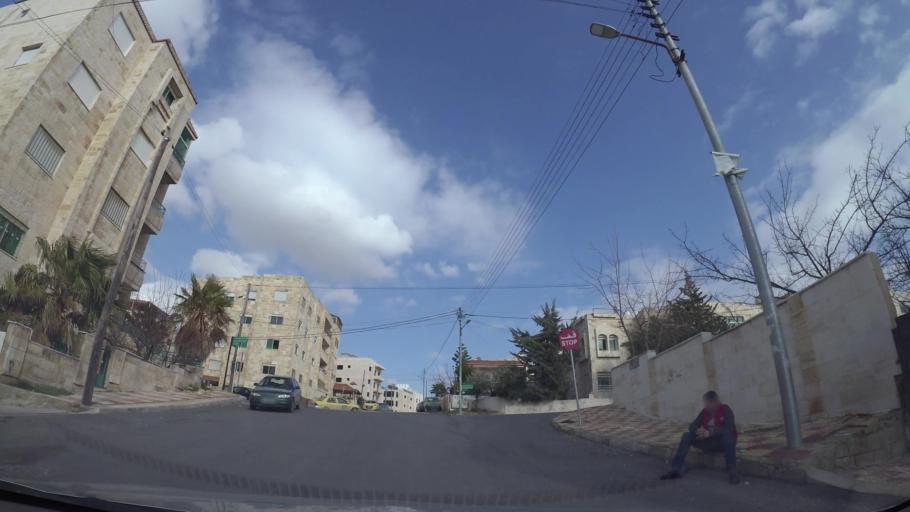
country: JO
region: Amman
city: Al Jubayhah
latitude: 32.0197
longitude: 35.8538
